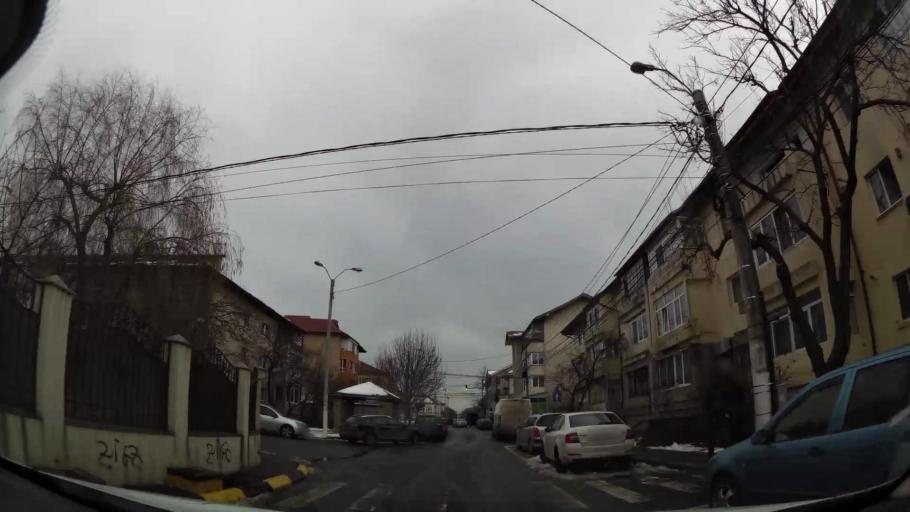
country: RO
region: Ilfov
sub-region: Comuna Otopeni
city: Otopeni
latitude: 44.5520
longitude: 26.0705
